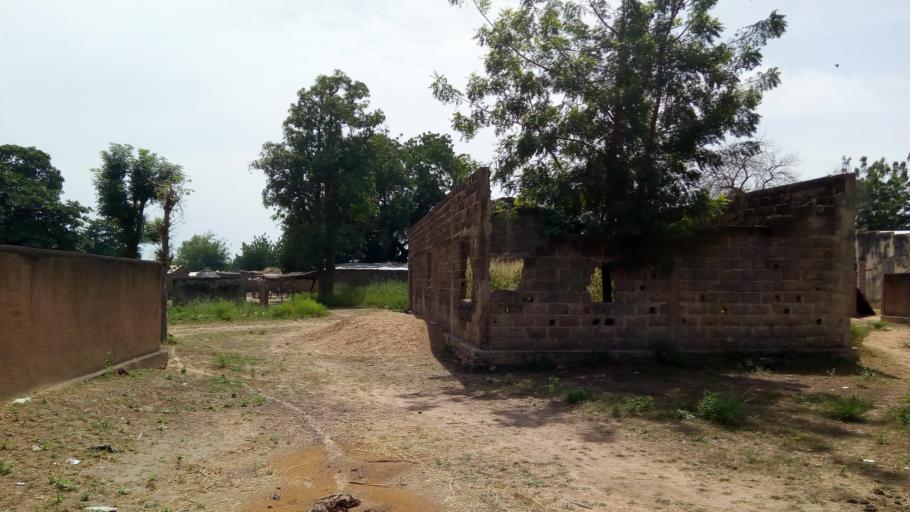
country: ML
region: Kayes
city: Kita
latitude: 13.4011
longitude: -8.8616
